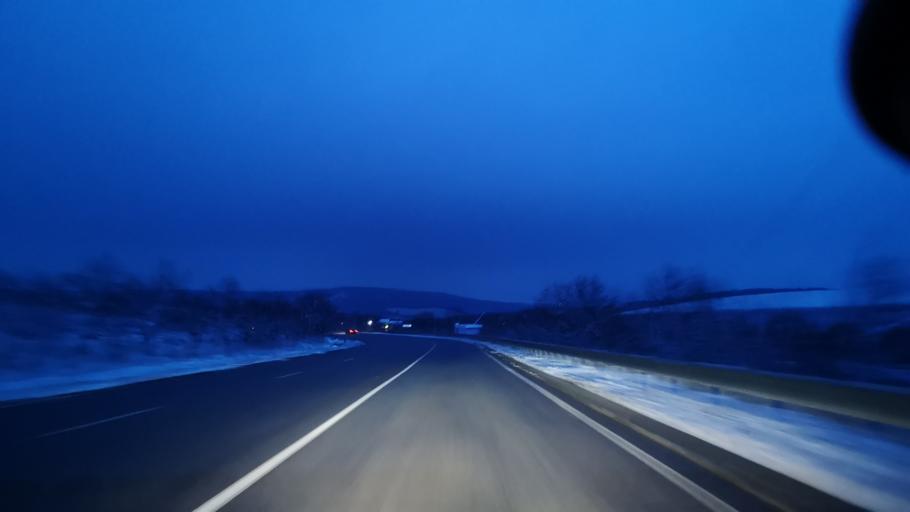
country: MD
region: Orhei
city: Orhei
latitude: 47.5259
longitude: 28.7962
